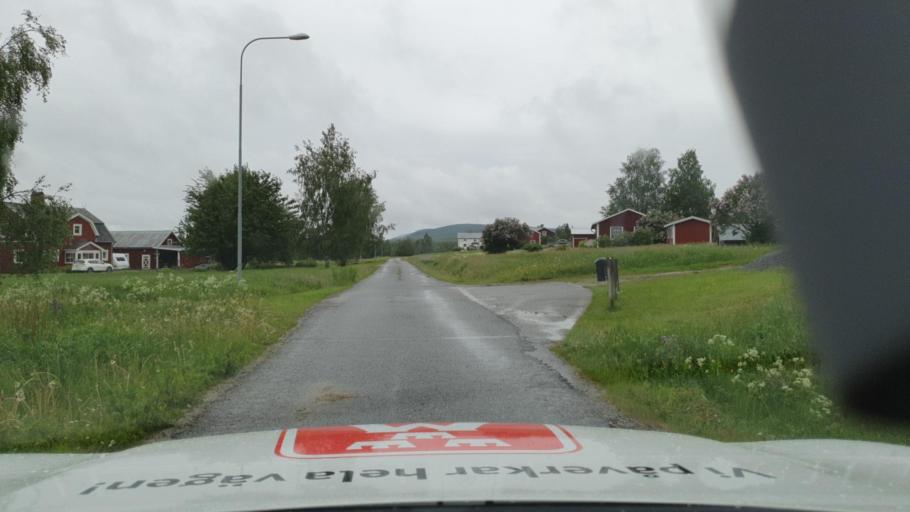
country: SE
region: Vaesterbotten
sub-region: Asele Kommun
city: Asele
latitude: 63.9410
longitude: 17.2709
